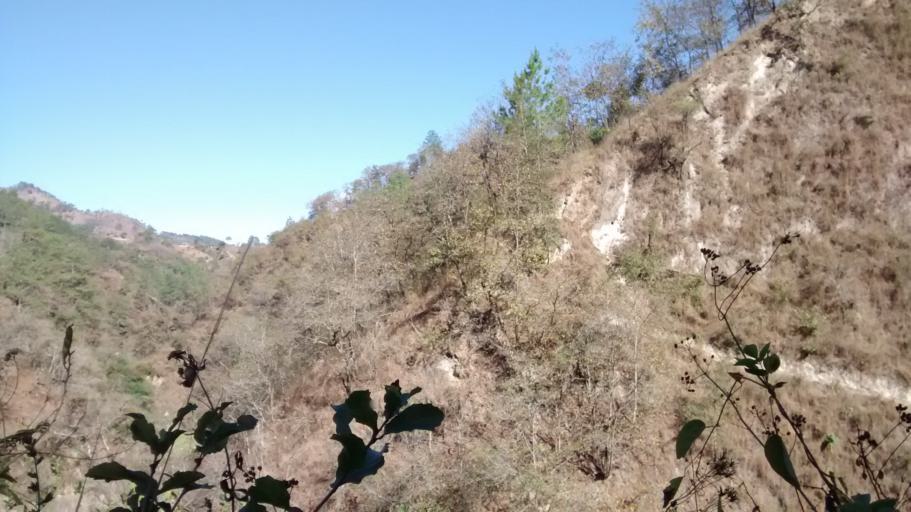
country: GT
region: Sacatepequez
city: Santo Domingo Xenacoj
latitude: 14.6796
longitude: -90.7217
